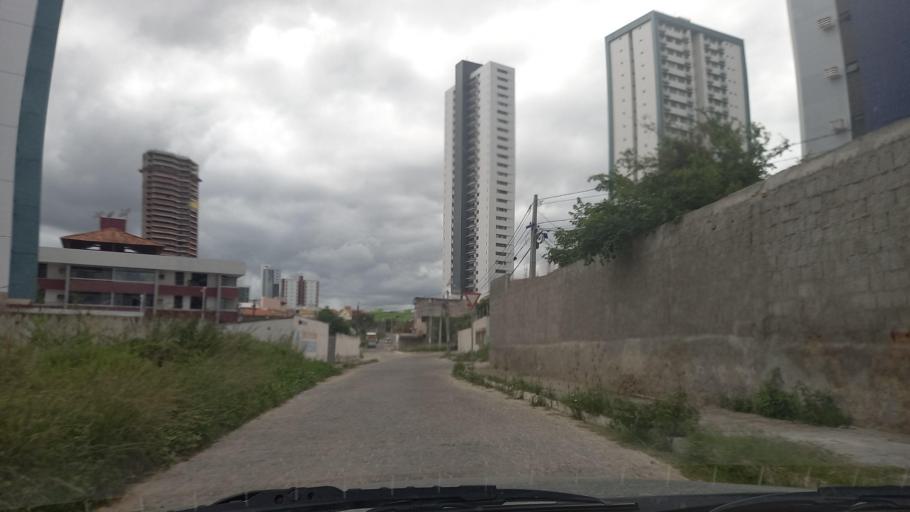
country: BR
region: Pernambuco
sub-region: Caruaru
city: Caruaru
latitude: -8.2675
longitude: -35.9674
